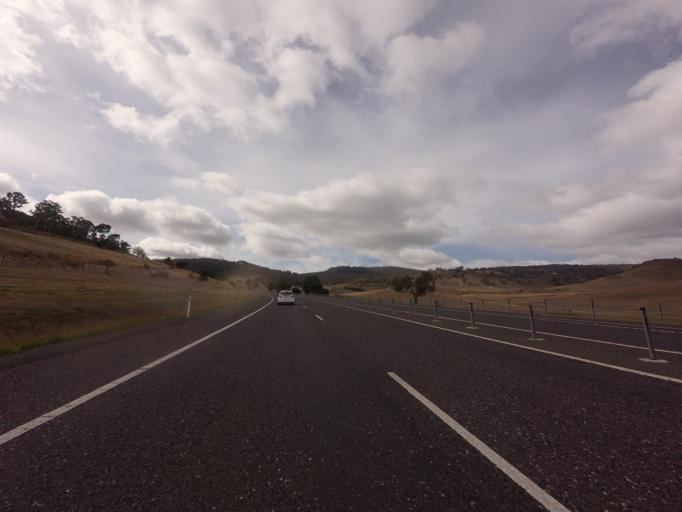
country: AU
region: Tasmania
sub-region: Brighton
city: Bridgewater
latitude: -42.4424
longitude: 147.2546
